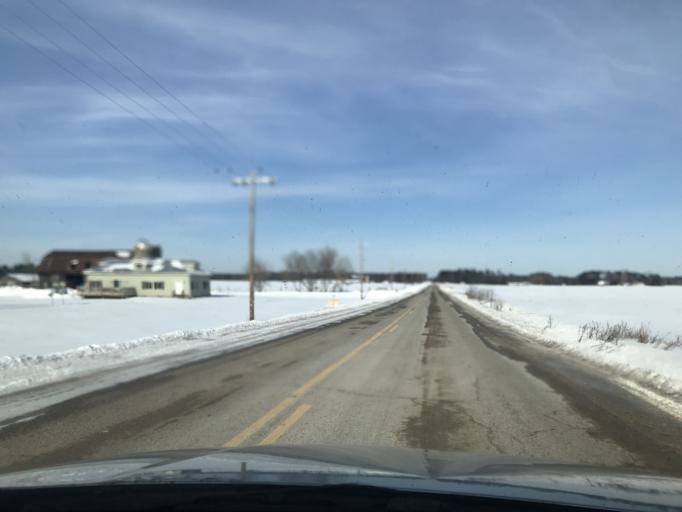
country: US
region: Wisconsin
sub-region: Oconto County
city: Oconto Falls
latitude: 45.1259
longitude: -88.1779
